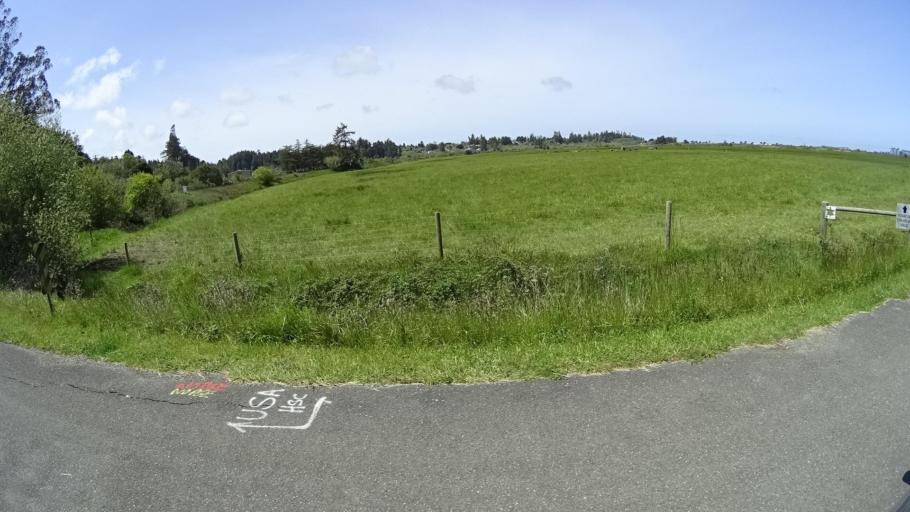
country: US
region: California
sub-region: Humboldt County
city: Myrtletown
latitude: 40.7877
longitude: -124.1089
